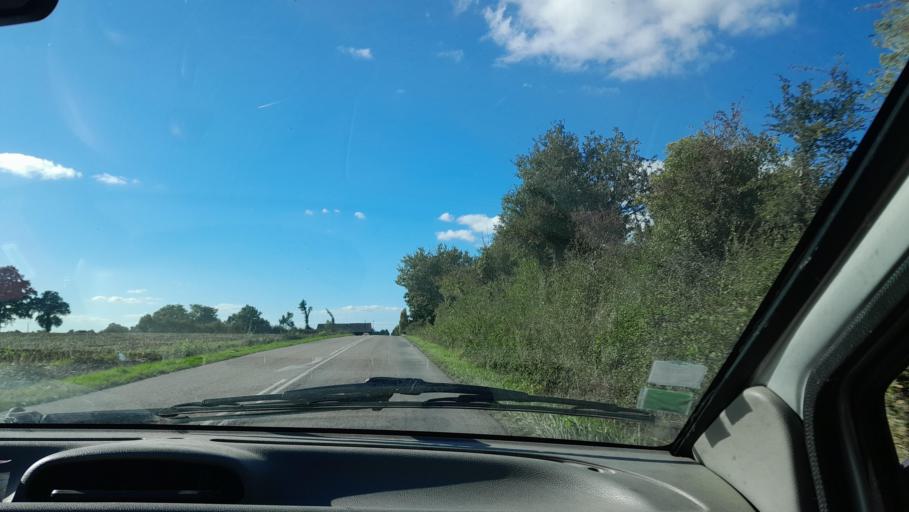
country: FR
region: Pays de la Loire
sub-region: Departement de la Mayenne
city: Quelaines-Saint-Gault
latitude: 47.9286
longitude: -0.8215
